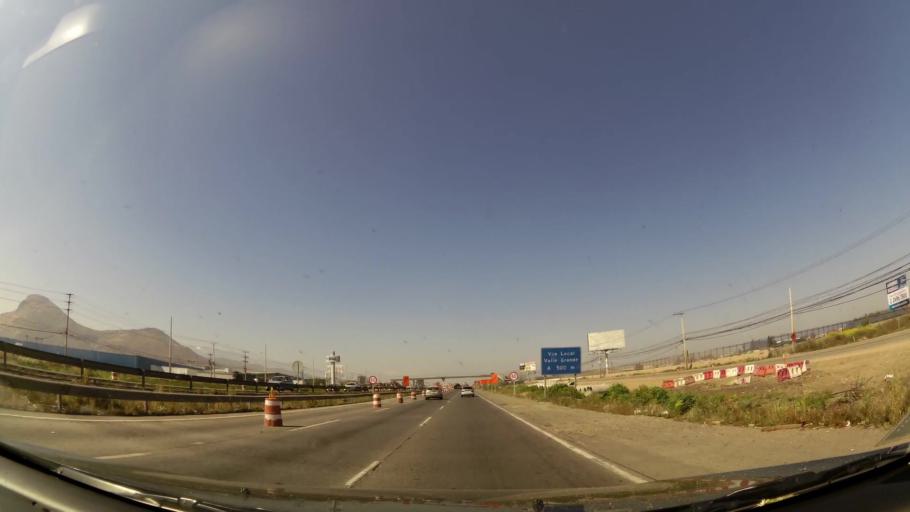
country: CL
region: Santiago Metropolitan
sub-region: Provincia de Chacabuco
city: Chicureo Abajo
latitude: -33.3070
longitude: -70.7270
